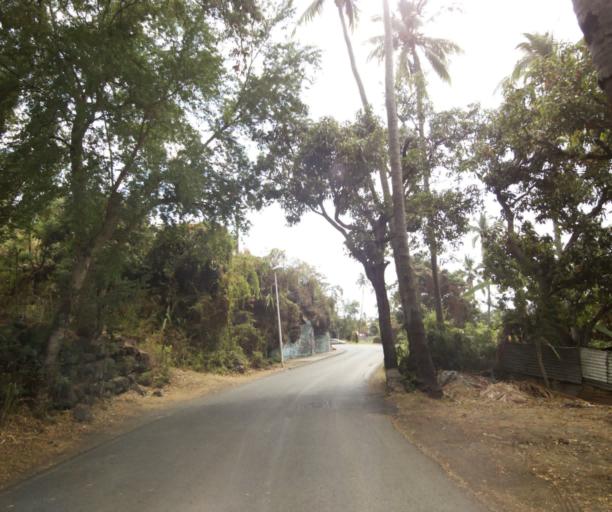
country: RE
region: Reunion
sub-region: Reunion
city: Saint-Paul
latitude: -21.0119
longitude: 55.2796
